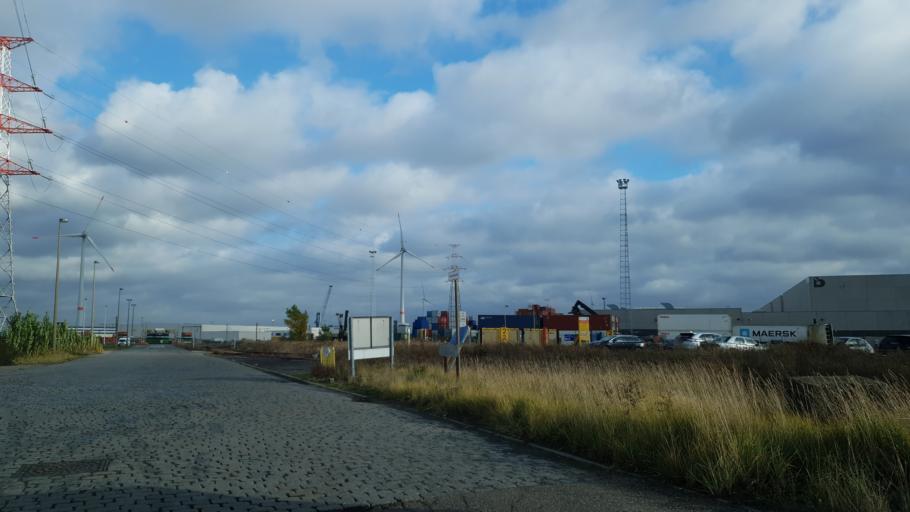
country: BE
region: Flanders
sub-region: Provincie Antwerpen
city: Zwijndrecht
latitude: 51.2629
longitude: 4.3593
